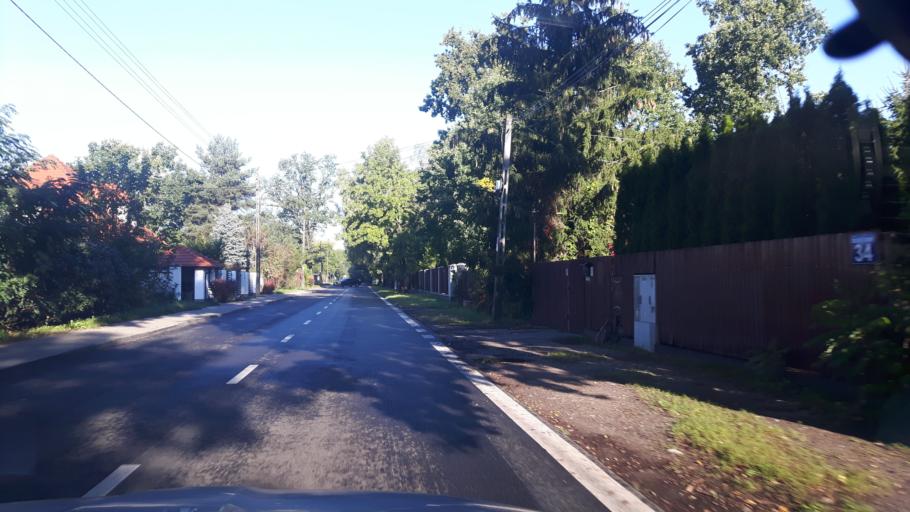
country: PL
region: Masovian Voivodeship
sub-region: Warszawa
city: Bialoleka
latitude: 52.3430
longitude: 20.9859
